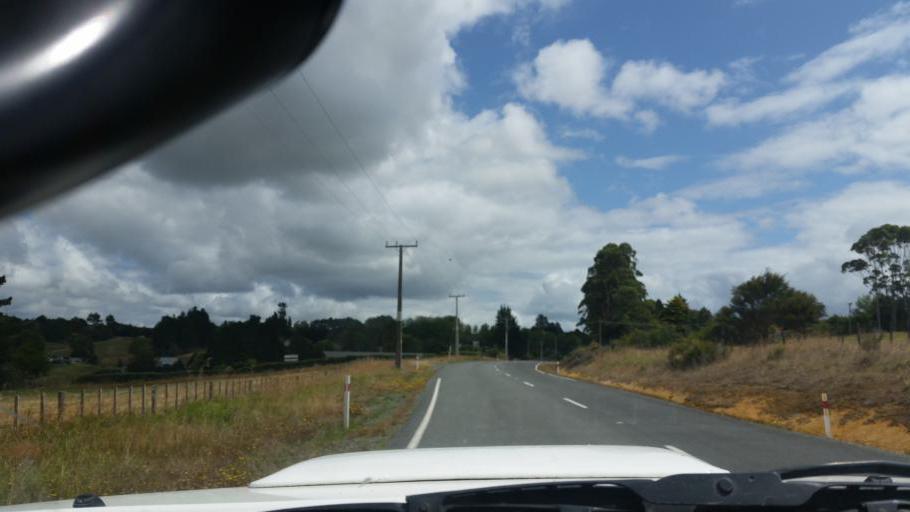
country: NZ
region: Auckland
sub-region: Auckland
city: Wellsford
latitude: -36.1345
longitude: 174.5571
